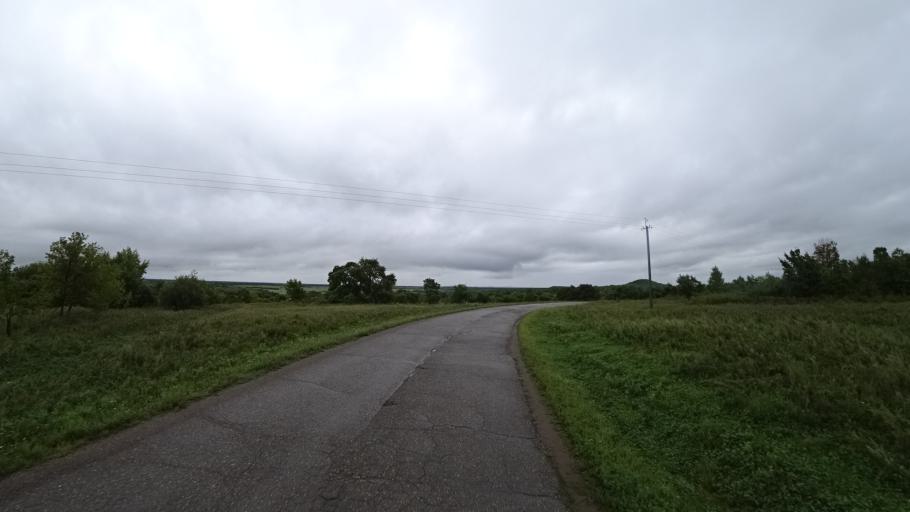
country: RU
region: Primorskiy
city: Monastyrishche
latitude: 44.2709
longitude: 132.4208
